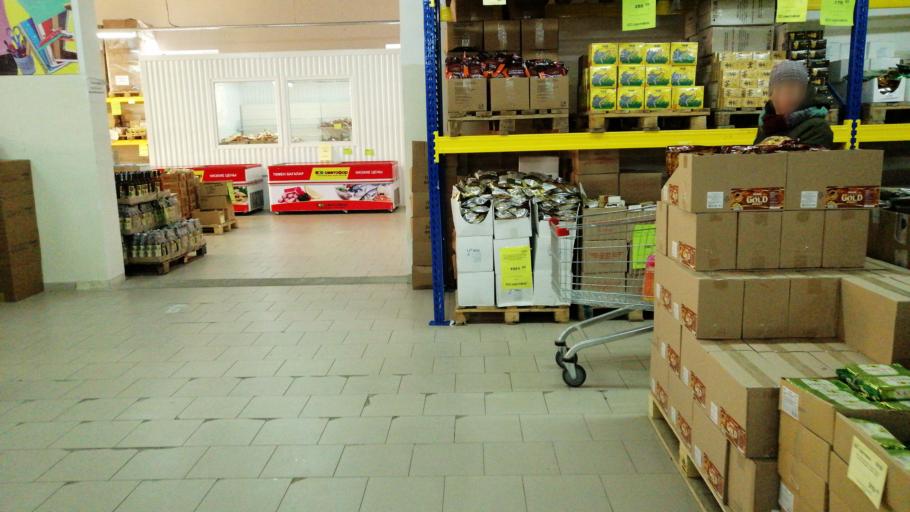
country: KZ
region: Aqtoebe
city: Aqtobe
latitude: 50.2915
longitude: 57.1976
